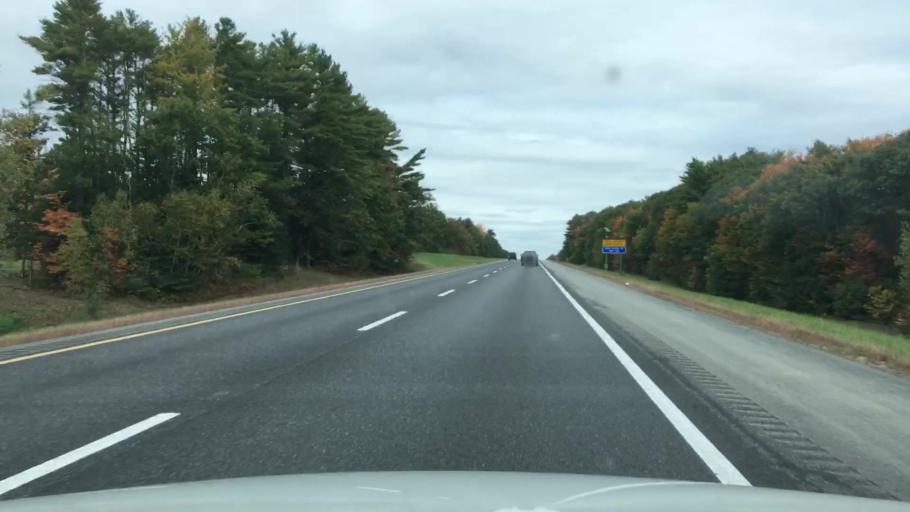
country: US
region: Maine
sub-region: Kennebec County
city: Gardiner
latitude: 44.1665
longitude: -69.8342
